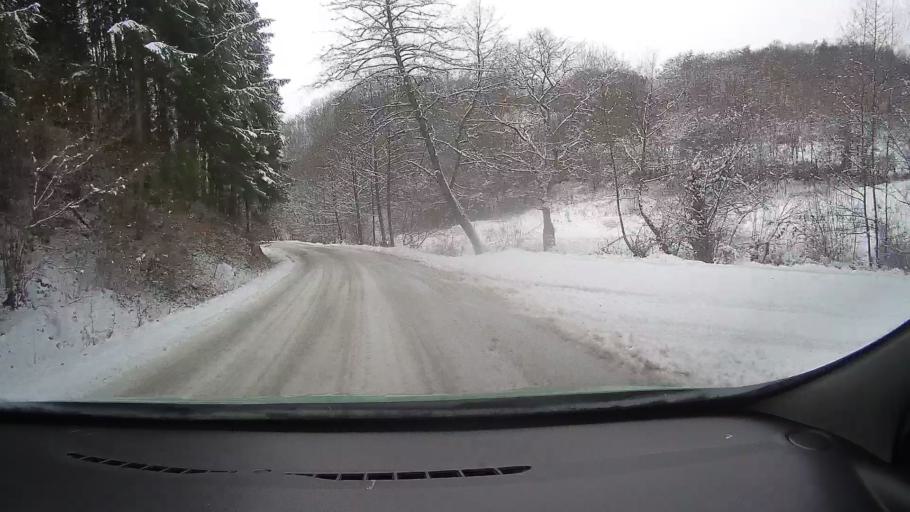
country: RO
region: Alba
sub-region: Comuna Almasu Mare
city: Almasu Mare
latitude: 46.0973
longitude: 23.1388
